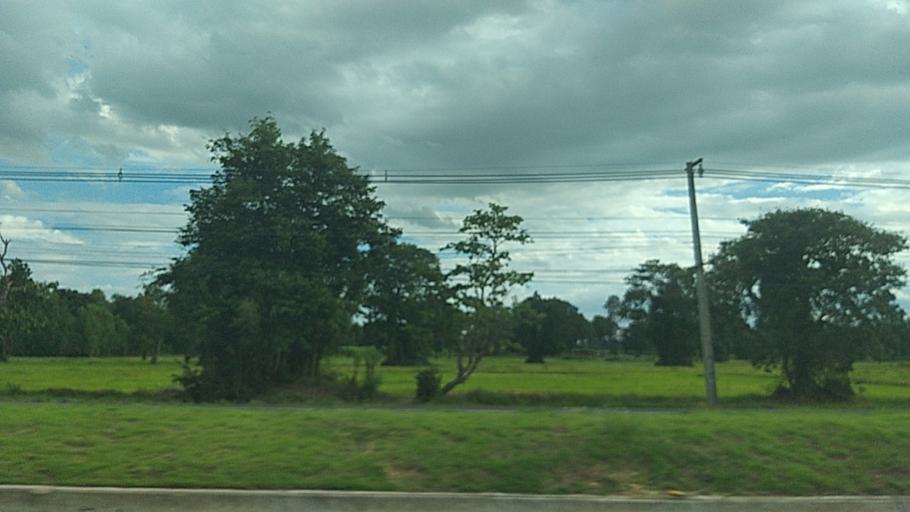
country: TH
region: Surin
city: Prasat
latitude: 14.5936
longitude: 103.4458
